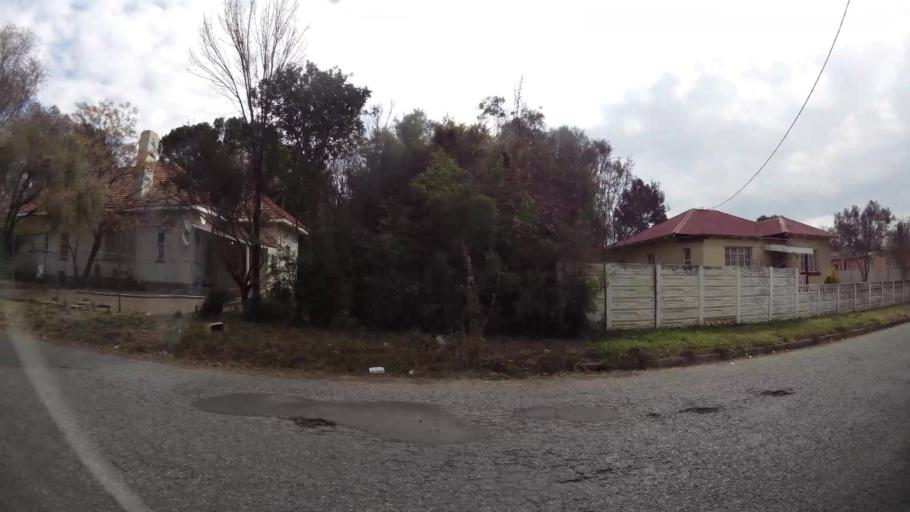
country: ZA
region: Orange Free State
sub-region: Fezile Dabi District Municipality
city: Kroonstad
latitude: -27.6560
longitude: 27.2337
